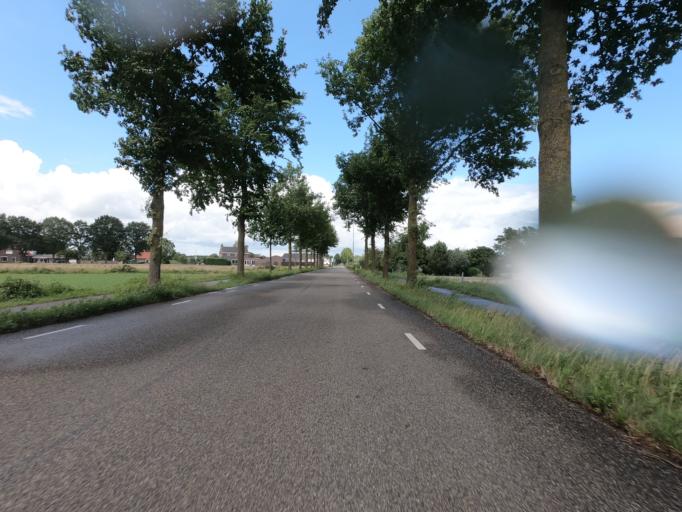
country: NL
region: North Brabant
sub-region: Gemeente Landerd
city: Zeeland
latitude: 51.7075
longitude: 5.6832
